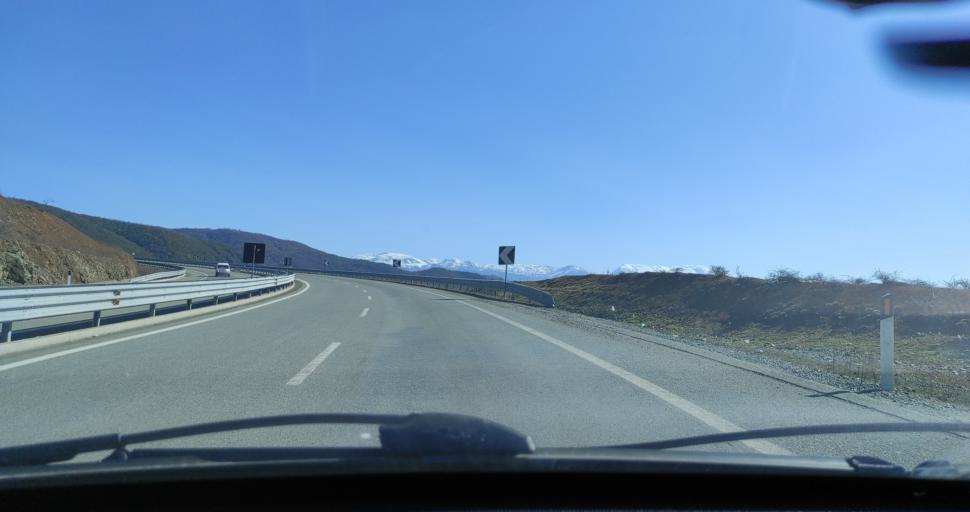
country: AL
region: Lezhe
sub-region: Rrethi i Mirdites
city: Rreshen
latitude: 41.7995
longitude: 19.9154
